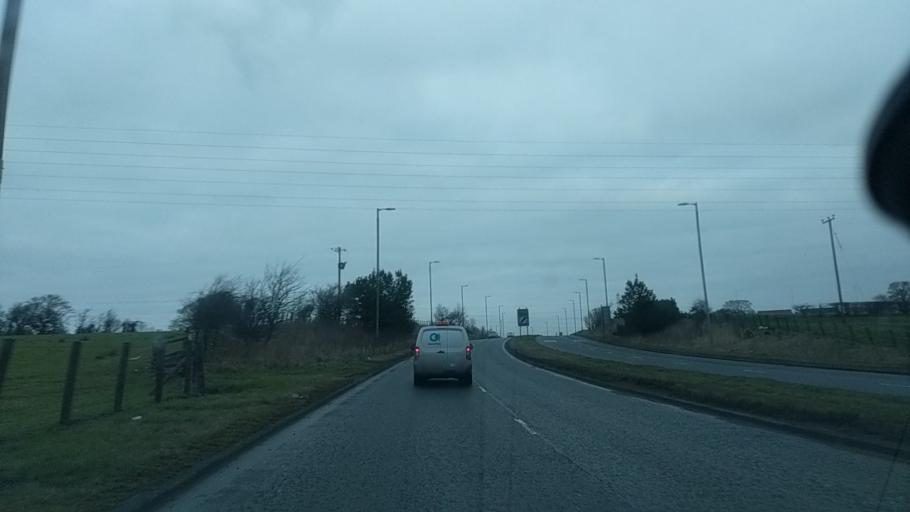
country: GB
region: Scotland
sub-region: South Lanarkshire
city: East Kilbride
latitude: 55.7865
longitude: -4.1668
